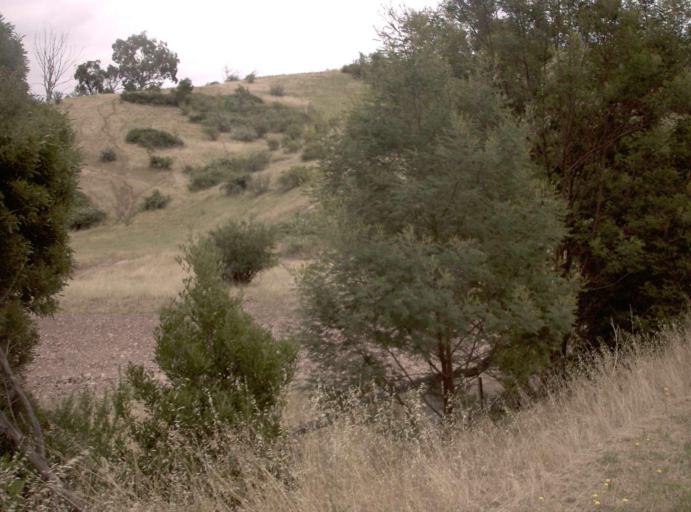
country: AU
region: Victoria
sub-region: Wellington
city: Heyfield
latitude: -37.6961
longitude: 146.6494
